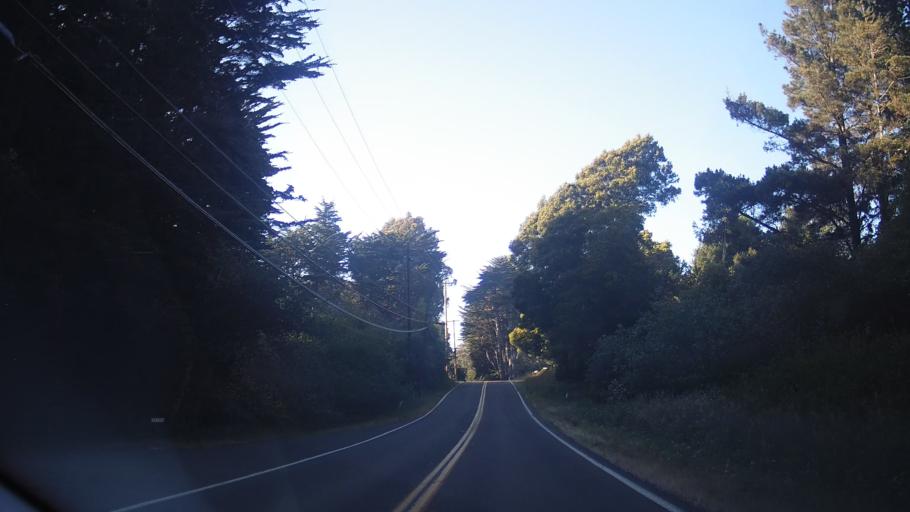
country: US
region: California
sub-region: Mendocino County
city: Fort Bragg
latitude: 39.5184
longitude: -123.7624
